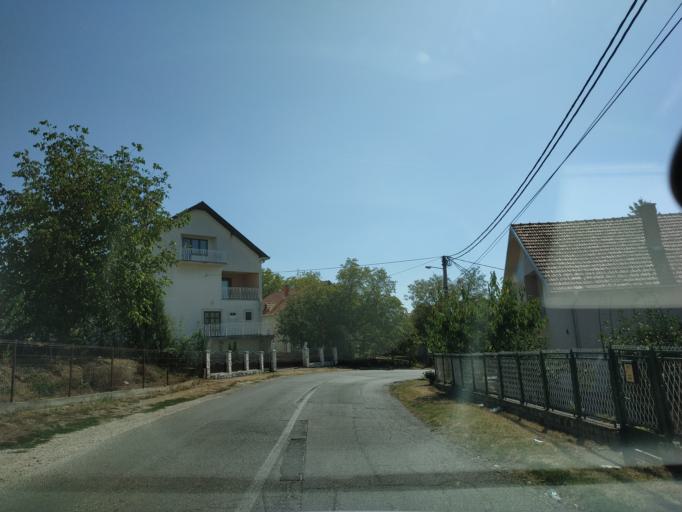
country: RS
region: Central Serbia
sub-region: Sumadijski Okrug
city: Topola
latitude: 44.2556
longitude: 20.6744
